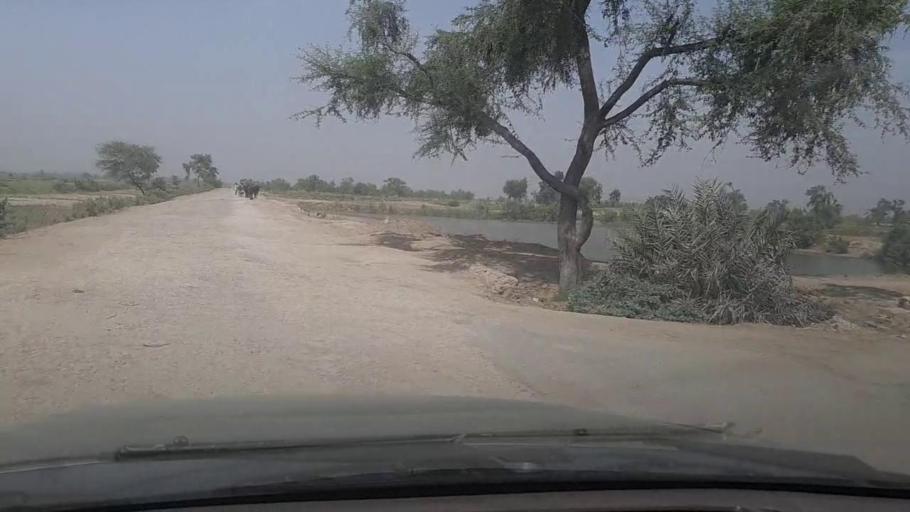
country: PK
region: Sindh
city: Madeji
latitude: 27.7969
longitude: 68.4461
